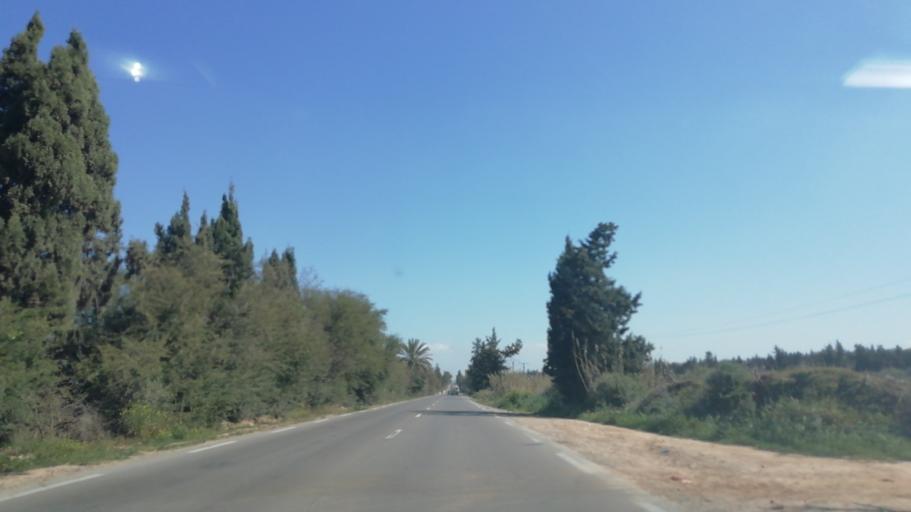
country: DZ
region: Mascara
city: Sig
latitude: 35.5745
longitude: -0.0110
